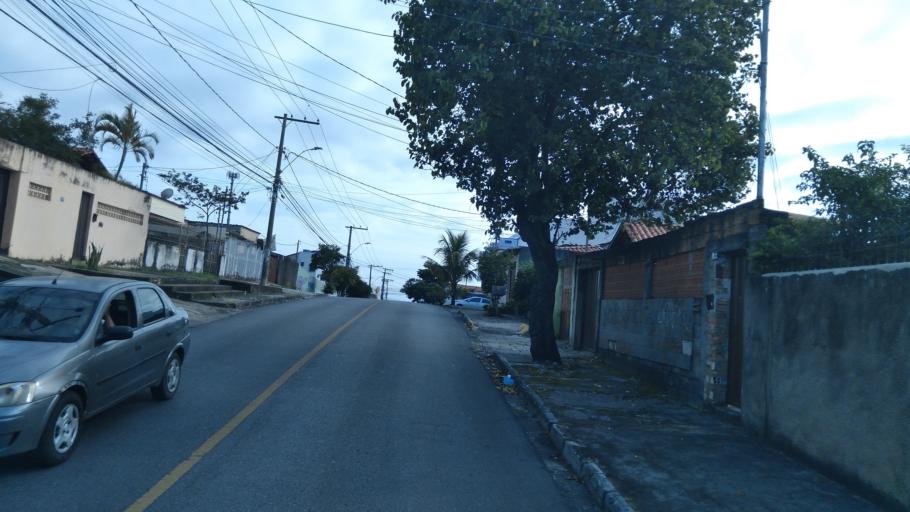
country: BR
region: Minas Gerais
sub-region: Belo Horizonte
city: Belo Horizonte
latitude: -19.8969
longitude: -43.9433
